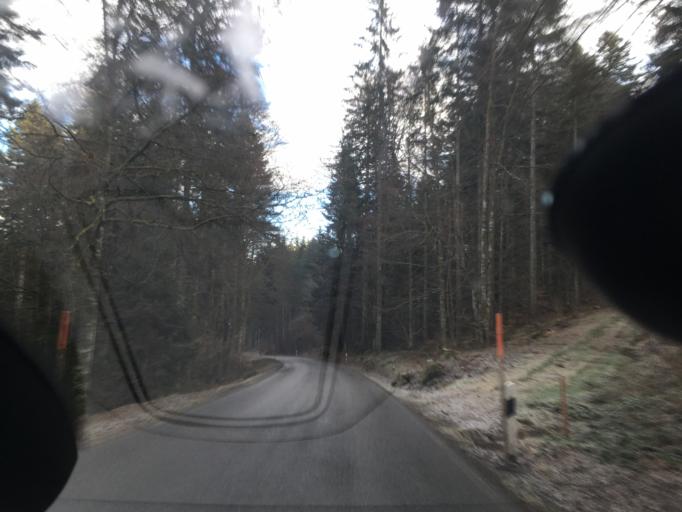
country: DE
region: Baden-Wuerttemberg
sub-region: Freiburg Region
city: Hausern
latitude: 47.7473
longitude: 8.1790
